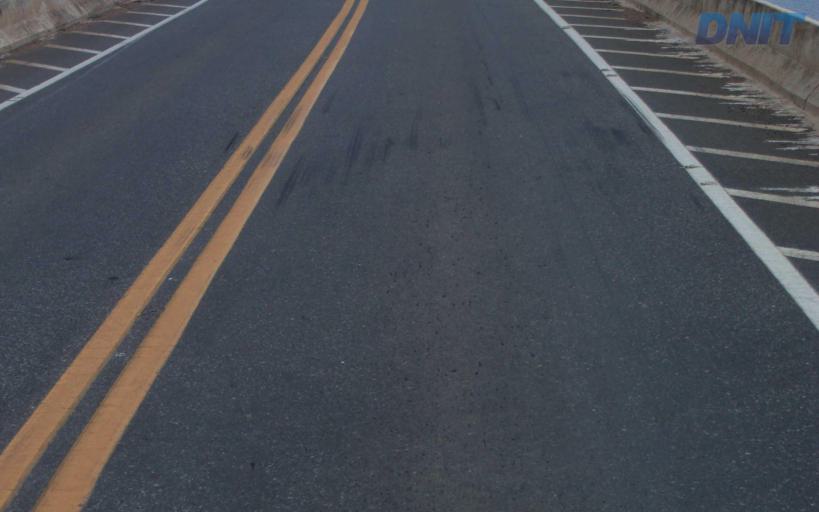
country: BR
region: Minas Gerais
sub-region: Governador Valadares
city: Governador Valadares
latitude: -19.0394
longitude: -42.1482
